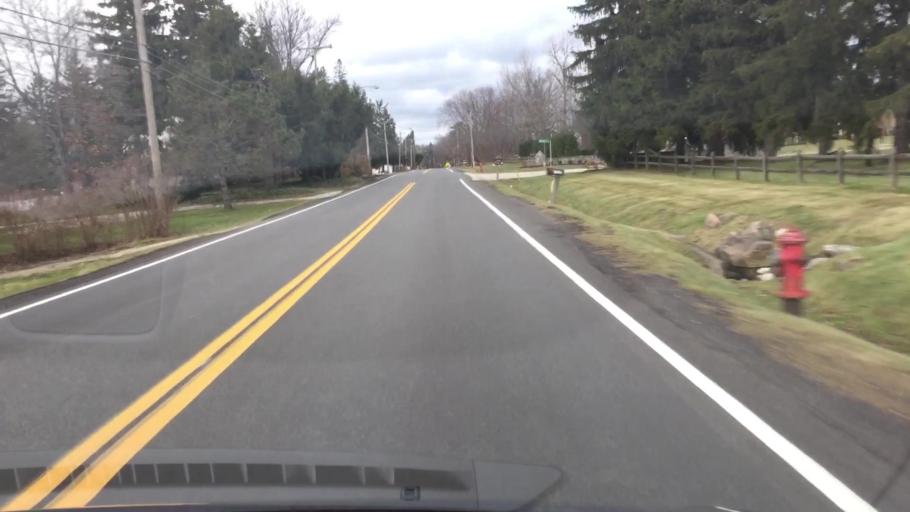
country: US
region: Ohio
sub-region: Summit County
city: Boston Heights
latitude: 41.2721
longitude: -81.5136
